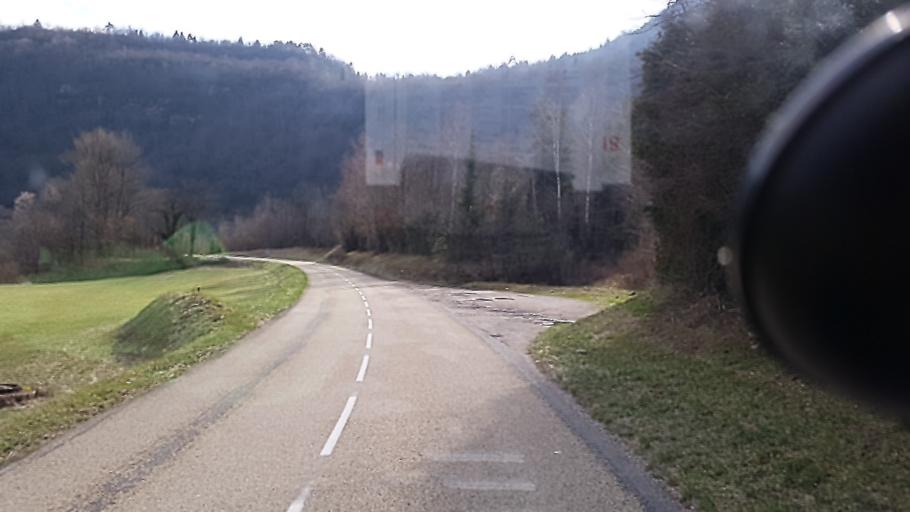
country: FR
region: Rhone-Alpes
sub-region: Departement de l'Ain
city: Dortan
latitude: 46.3275
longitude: 5.6440
